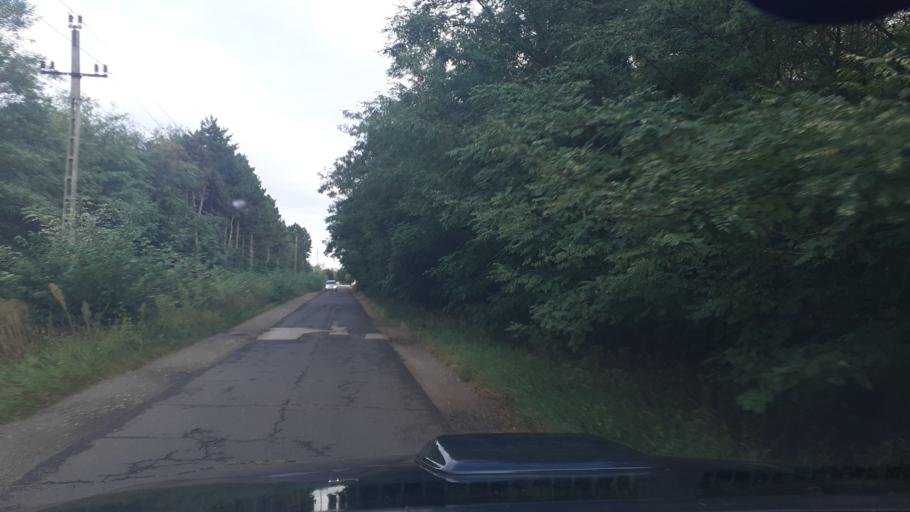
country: HU
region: Fejer
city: dunaujvaros
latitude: 46.9473
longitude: 18.8607
